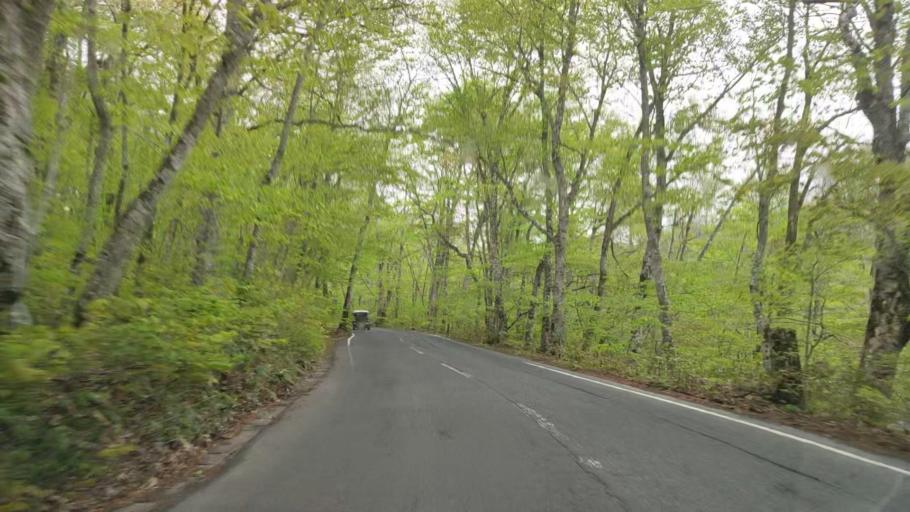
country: JP
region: Aomori
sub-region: Aomori Shi
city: Furudate
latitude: 40.5566
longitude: 140.9710
